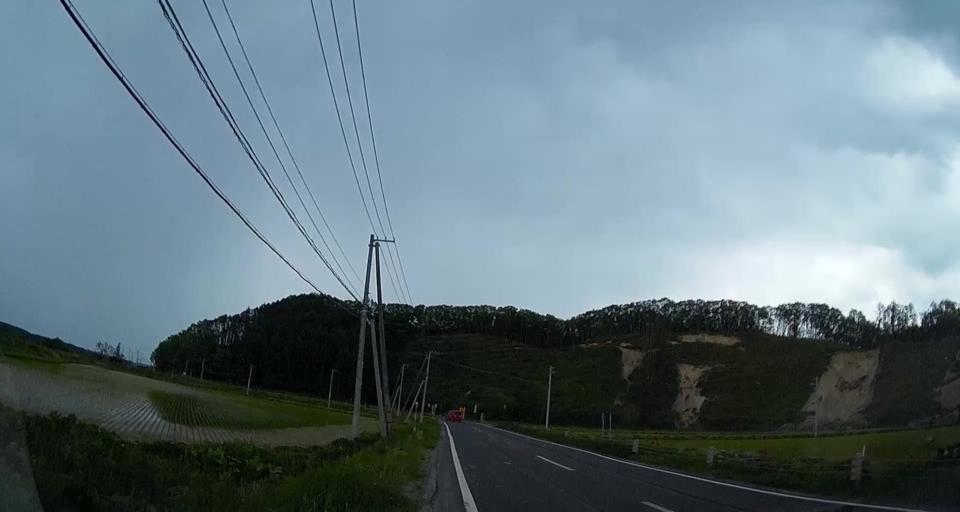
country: JP
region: Hokkaido
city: Chitose
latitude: 42.7568
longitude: 141.9174
